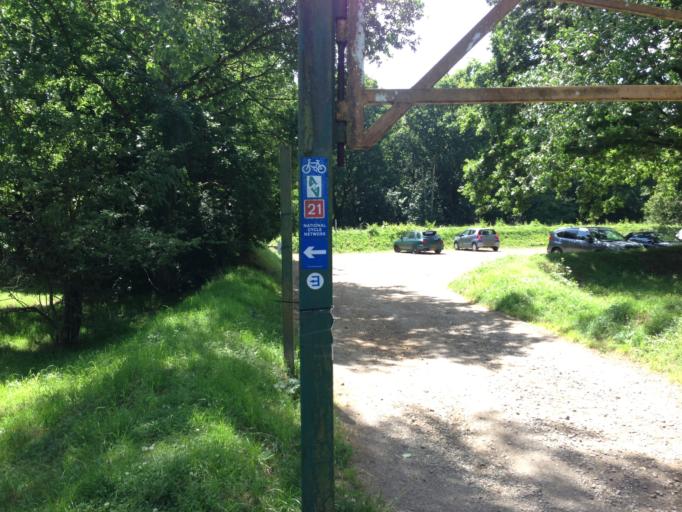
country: GB
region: England
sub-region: Surrey
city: Horley
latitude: 51.1640
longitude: -0.1682
